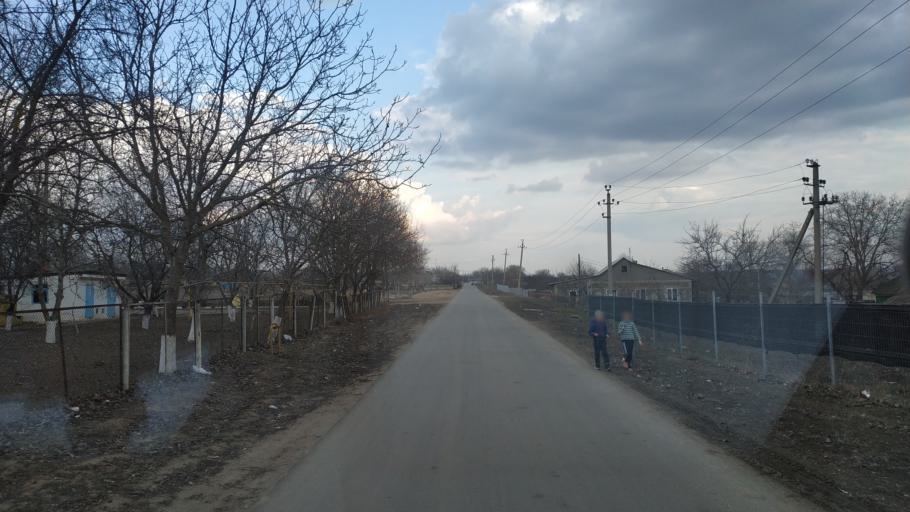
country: MD
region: Telenesti
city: Grigoriopol
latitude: 47.0099
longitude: 29.2952
